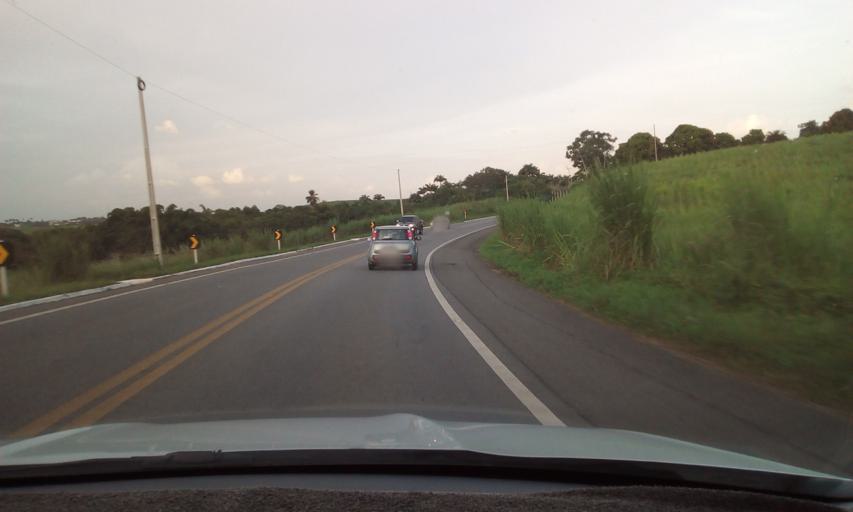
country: BR
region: Pernambuco
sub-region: Vicencia
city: Vicencia
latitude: -7.6297
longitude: -35.2499
